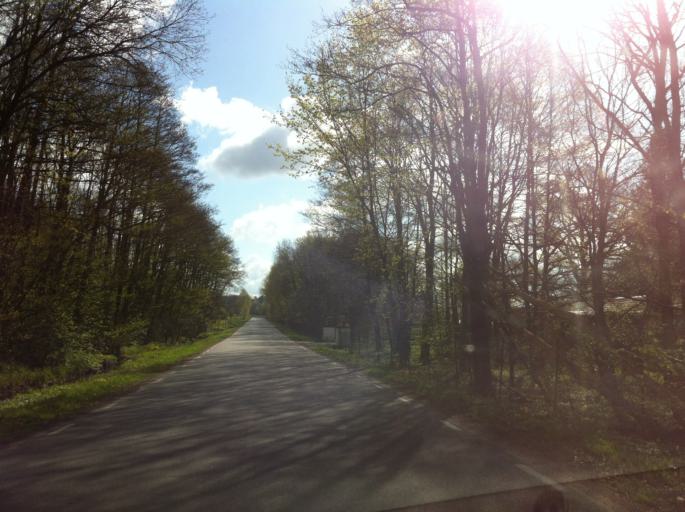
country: SE
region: Skane
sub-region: Hoors Kommun
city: Hoeoer
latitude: 55.9045
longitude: 13.5086
